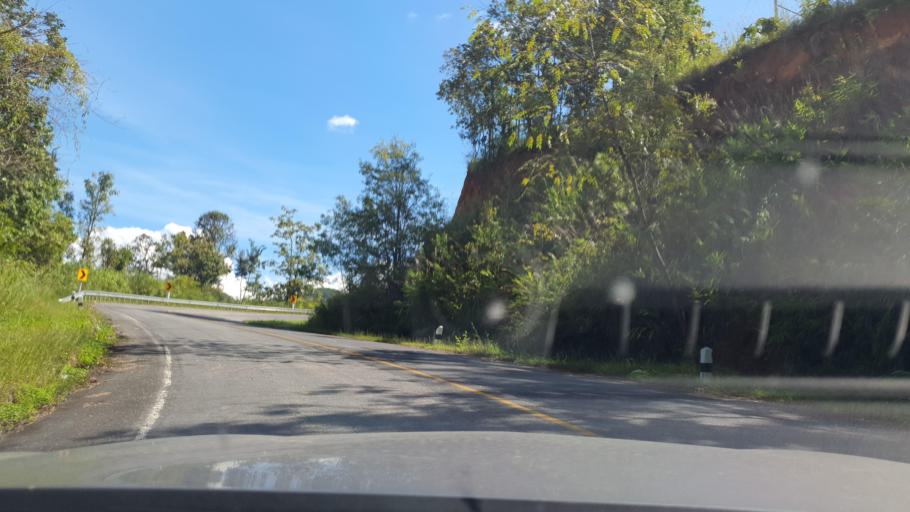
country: TH
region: Chiang Mai
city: Phrao
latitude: 19.3576
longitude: 99.2732
